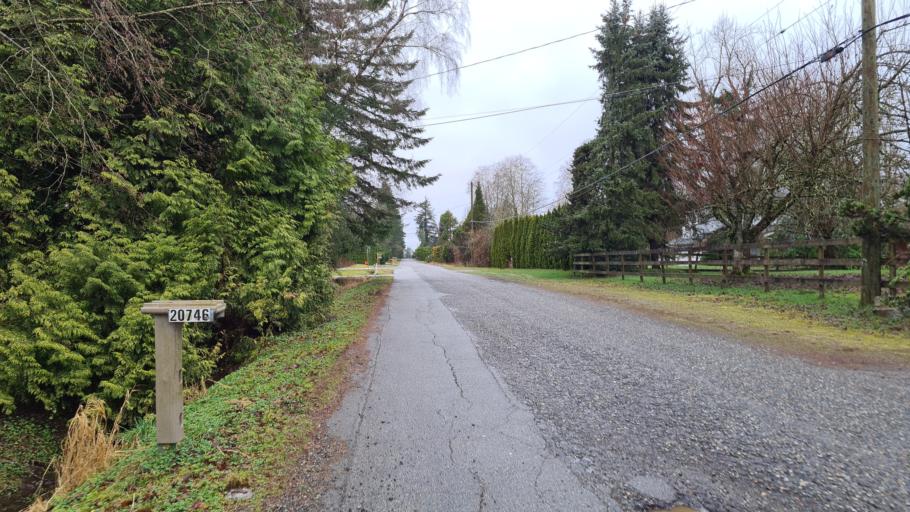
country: CA
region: British Columbia
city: Walnut Grove
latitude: 49.1383
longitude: -122.6484
